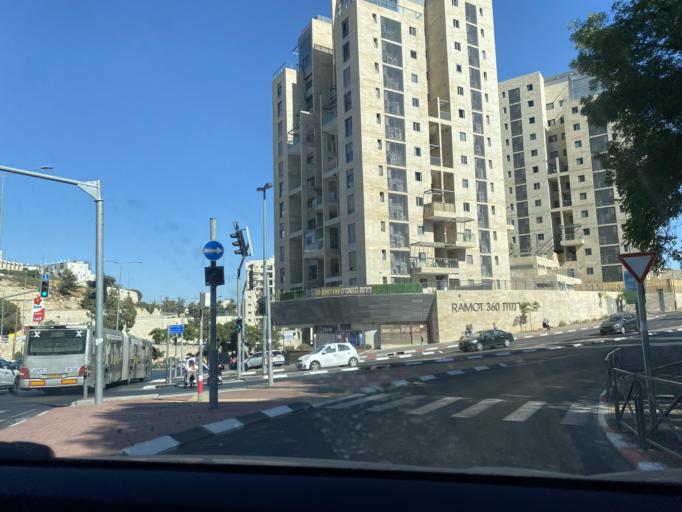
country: PS
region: West Bank
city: Bayt Iksa
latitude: 31.8188
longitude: 35.1936
